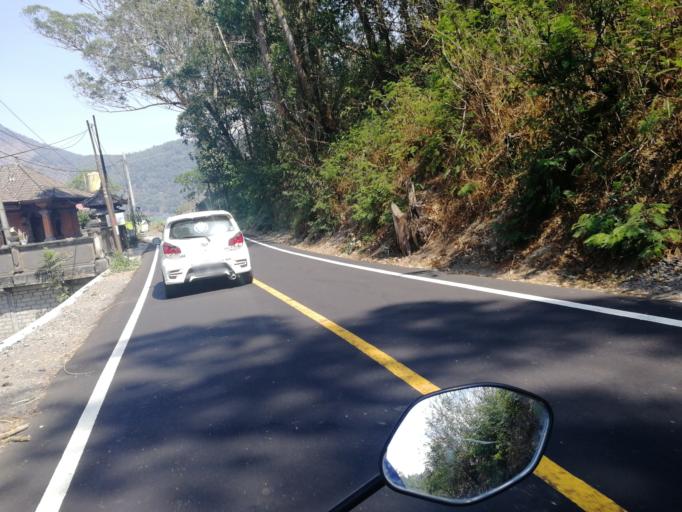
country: ID
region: Bali
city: Banjar Kedisan
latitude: -8.2770
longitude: 115.3783
